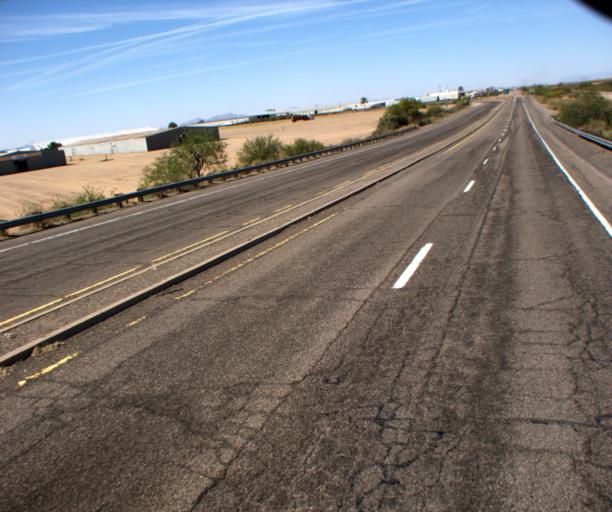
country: US
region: Arizona
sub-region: Pinal County
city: Eloy
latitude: 32.7285
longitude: -111.5158
